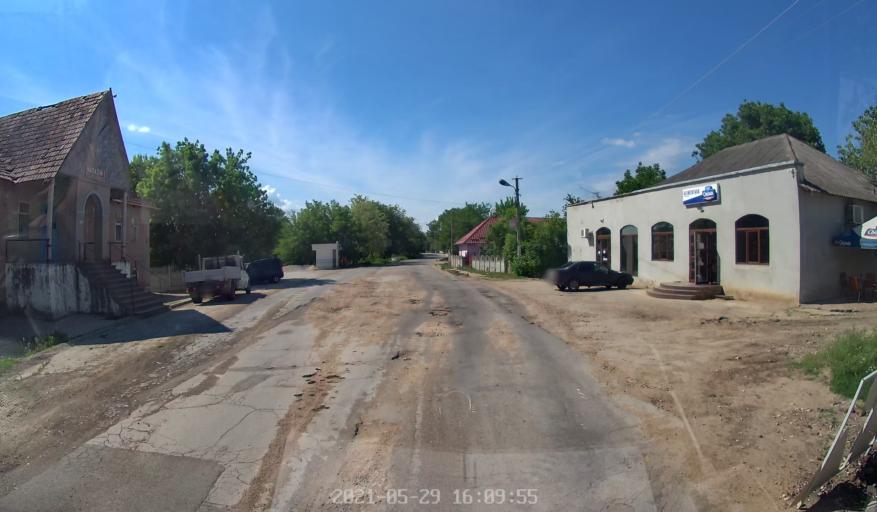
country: MD
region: Chisinau
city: Singera
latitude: 46.8219
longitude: 28.8794
